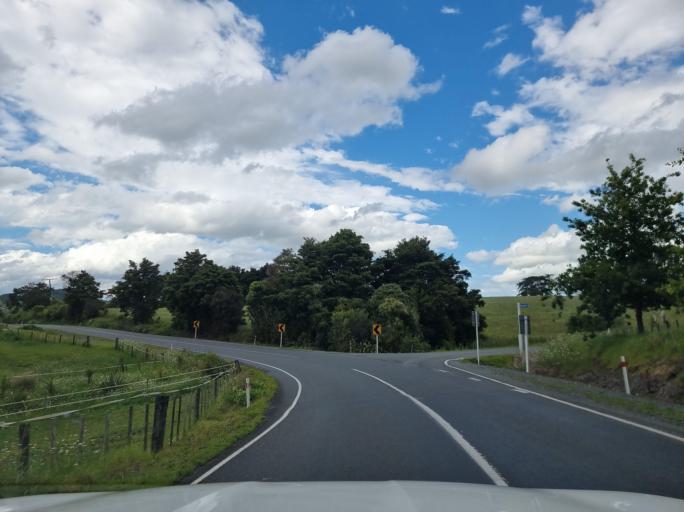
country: NZ
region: Northland
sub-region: Whangarei
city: Maungatapere
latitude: -35.8531
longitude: 174.2618
